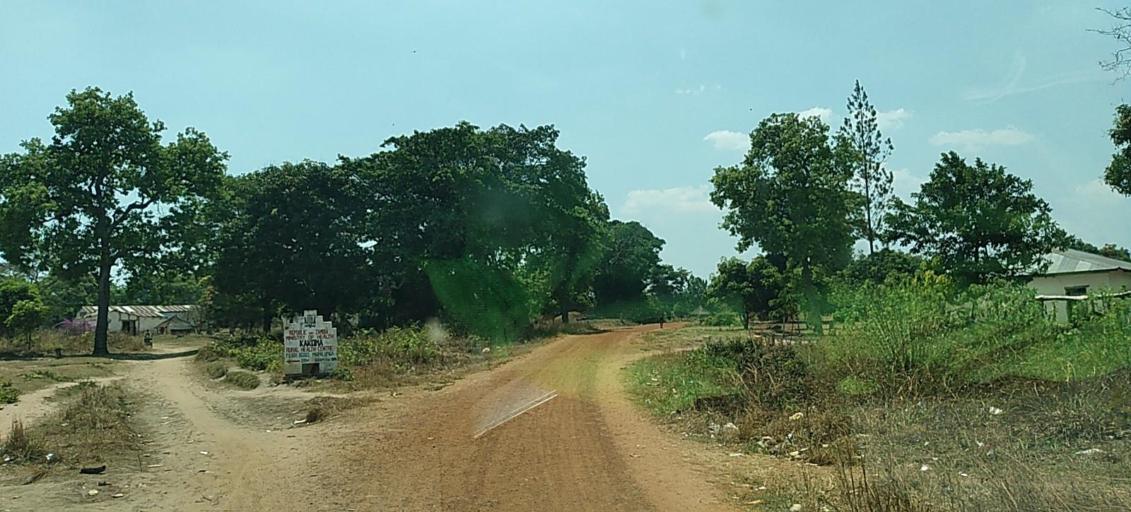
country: CD
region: Katanga
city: Kolwezi
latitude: -11.2970
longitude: 25.2110
